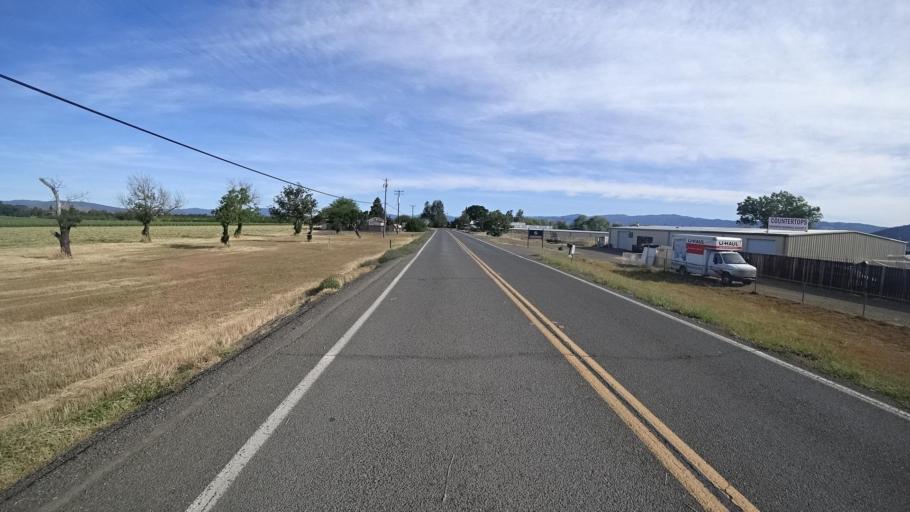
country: US
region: California
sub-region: Lake County
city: Kelseyville
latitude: 38.9827
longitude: -122.8461
